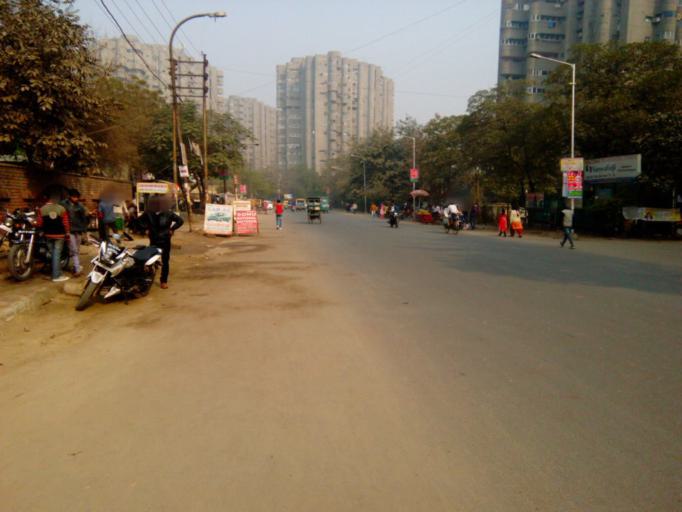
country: IN
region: Uttar Pradesh
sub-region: Gautam Buddha Nagar
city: Noida
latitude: 28.6420
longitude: 77.3194
